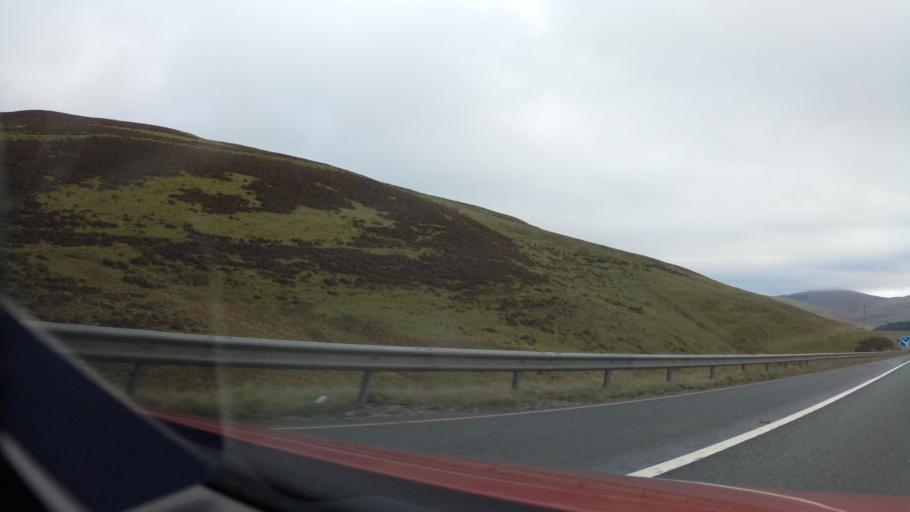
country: GB
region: Scotland
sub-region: South Lanarkshire
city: Douglas
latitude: 55.5192
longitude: -3.7212
